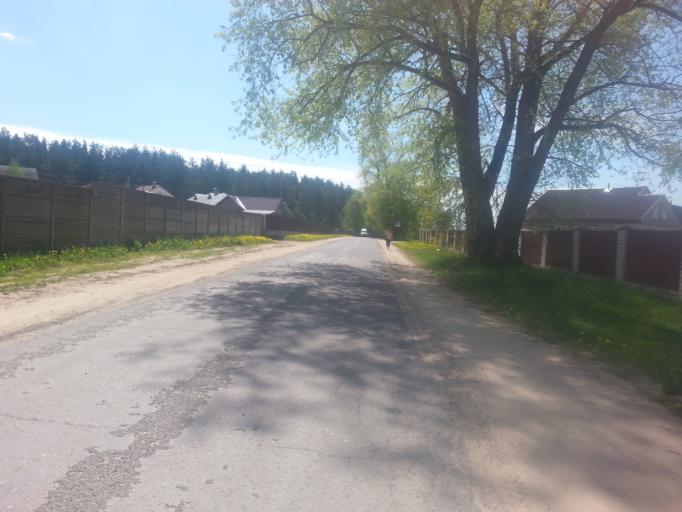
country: BY
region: Minsk
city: Narach
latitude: 54.9259
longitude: 26.6915
